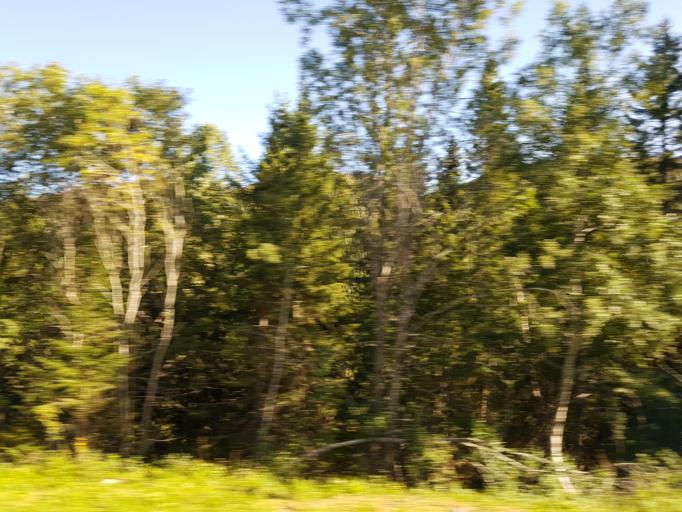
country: NO
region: Sor-Trondelag
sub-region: Afjord
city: A i Afjord
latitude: 63.7221
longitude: 10.2329
